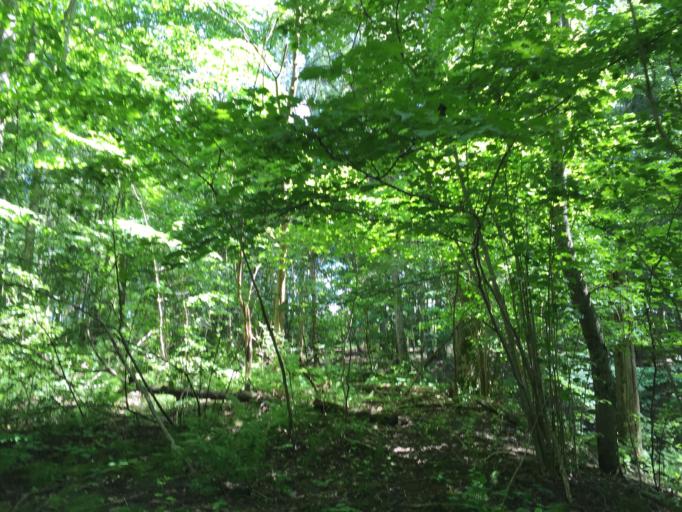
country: LV
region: Sigulda
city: Sigulda
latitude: 57.1887
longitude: 24.9330
